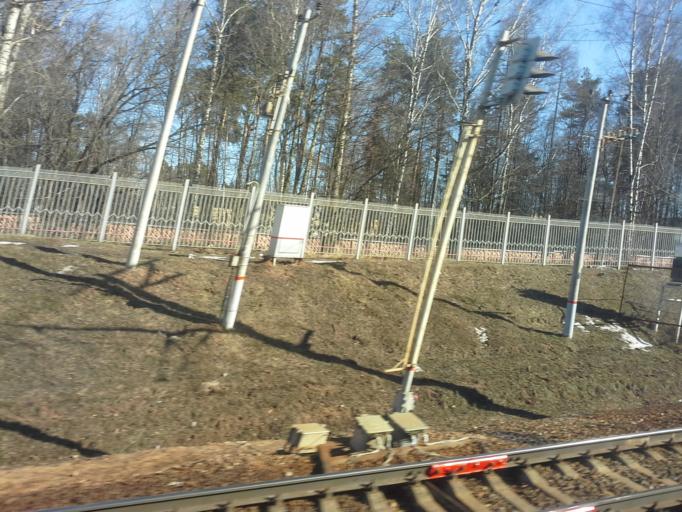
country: RU
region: Moskovskaya
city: Mamontovka
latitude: 55.9899
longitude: 37.8262
